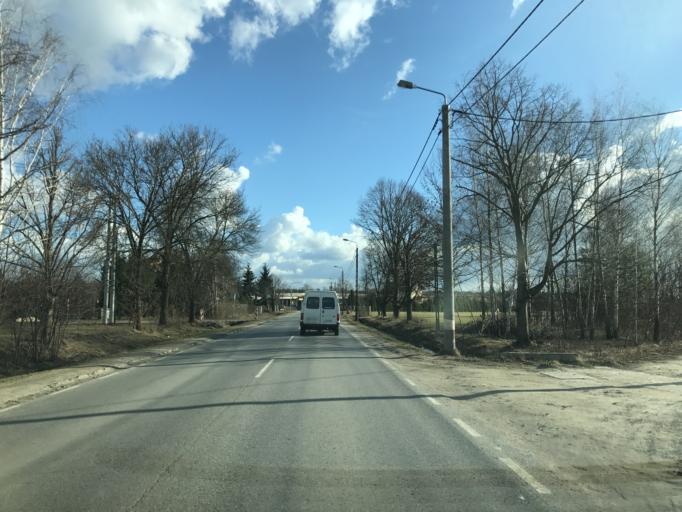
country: PL
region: Masovian Voivodeship
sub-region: Powiat wolominski
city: Radzymin
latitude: 52.3957
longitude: 21.1974
